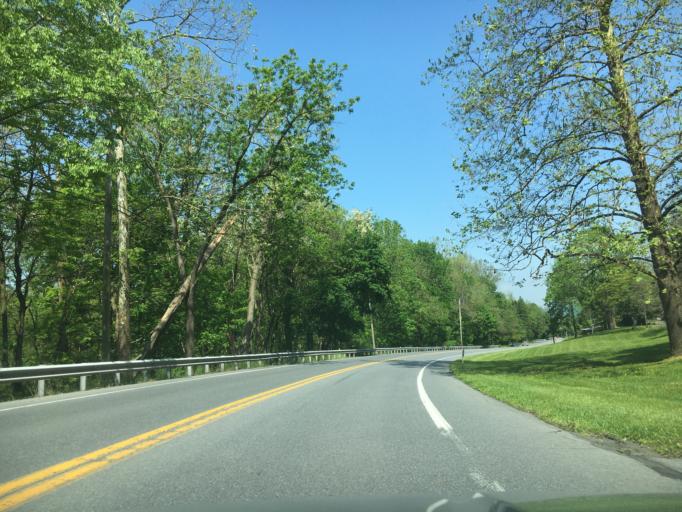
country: US
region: Pennsylvania
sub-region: Berks County
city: Oley
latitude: 40.3741
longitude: -75.7196
